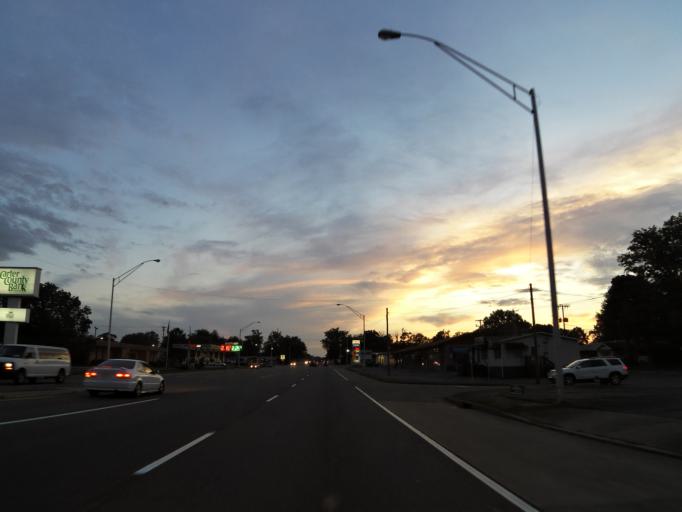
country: US
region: Tennessee
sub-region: Carter County
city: Elizabethton
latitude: 36.3525
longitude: -82.2097
